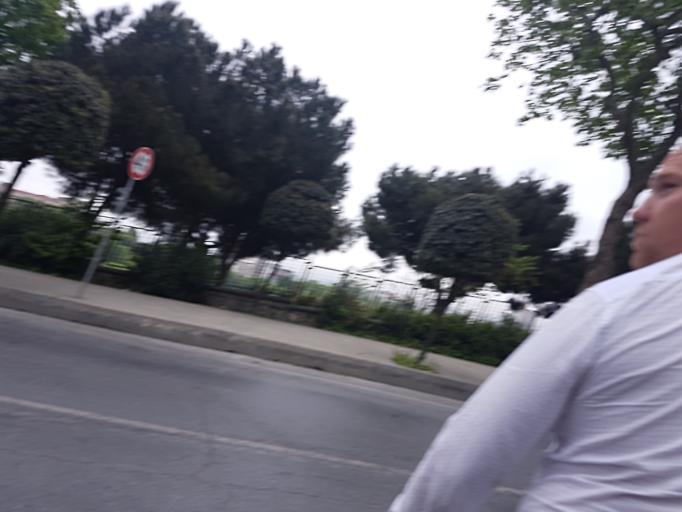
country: TR
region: Istanbul
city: Sisli
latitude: 41.0441
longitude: 28.9905
